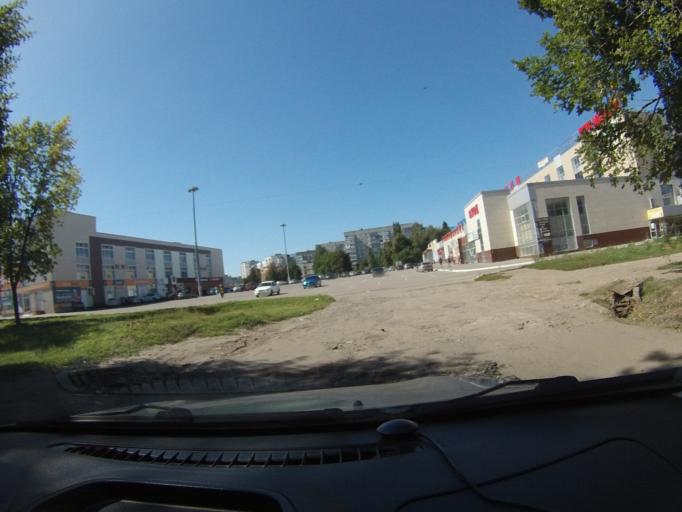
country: RU
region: Tambov
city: Tambov
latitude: 52.7591
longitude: 41.4386
